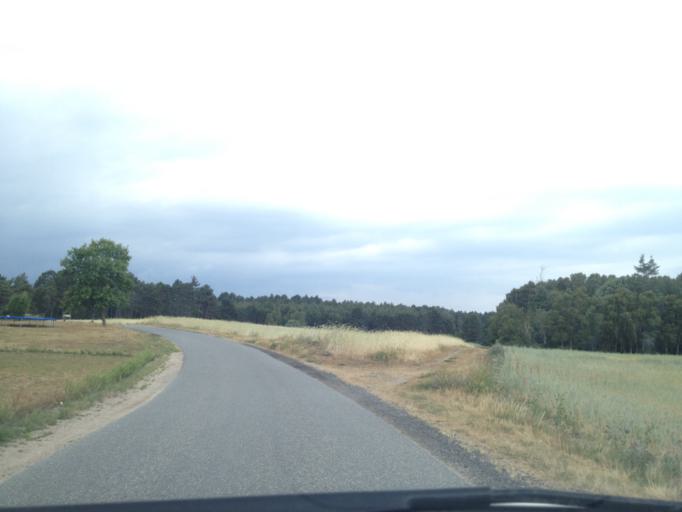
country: DK
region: Central Jutland
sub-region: Syddjurs Kommune
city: Ebeltoft
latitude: 56.1592
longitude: 10.6928
